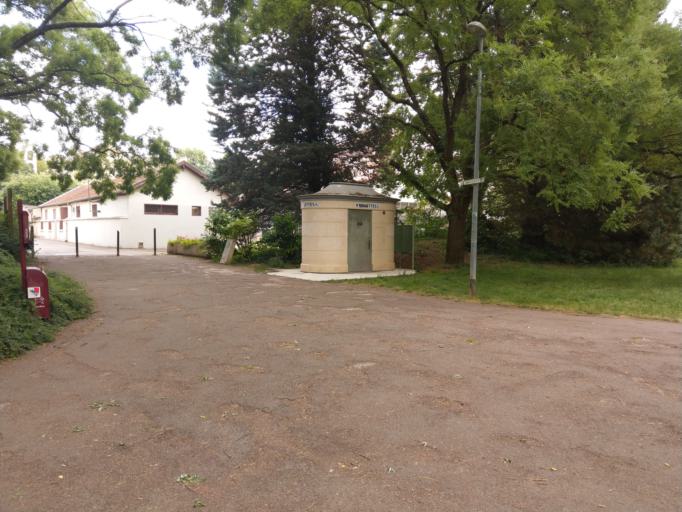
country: FR
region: Bourgogne
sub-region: Departement de la Cote-d'Or
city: Dijon
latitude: 47.3186
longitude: 5.0246
